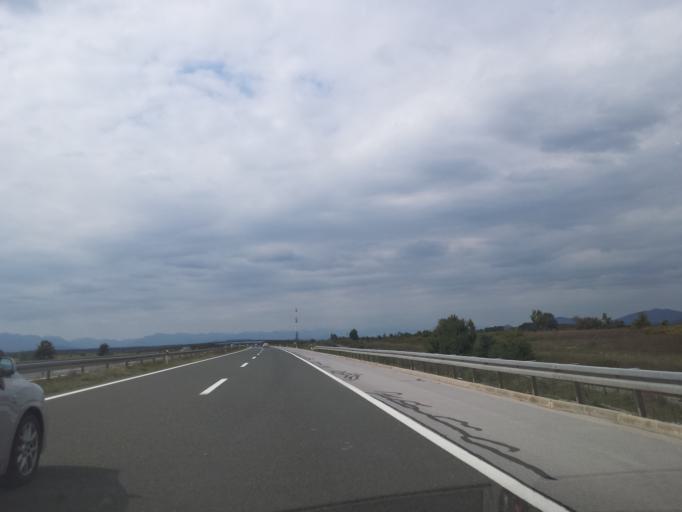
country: HR
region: Licko-Senjska
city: Gospic
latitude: 44.4777
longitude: 15.5725
